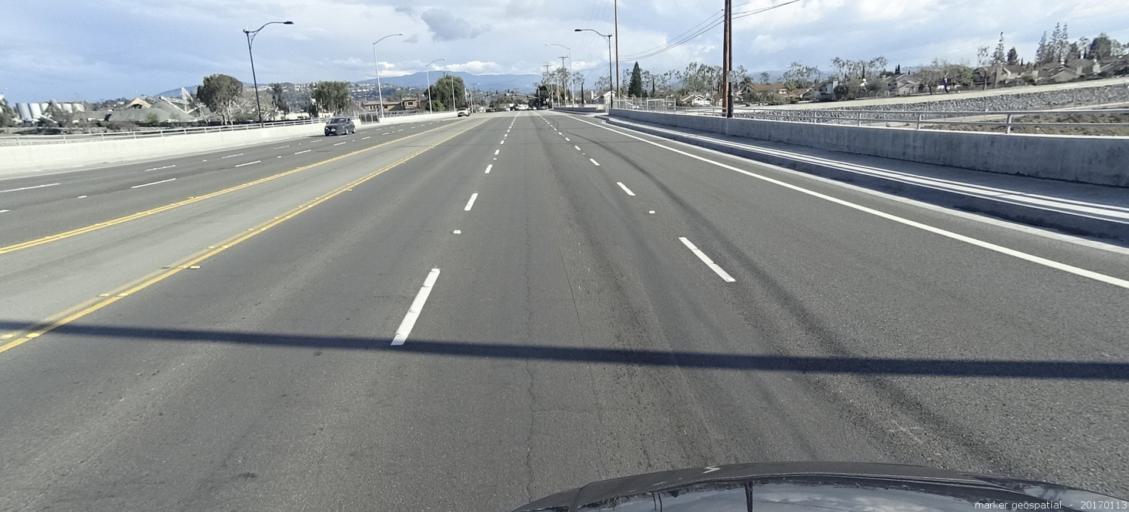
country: US
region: California
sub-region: Orange County
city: Placentia
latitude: 33.8356
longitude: -117.8644
